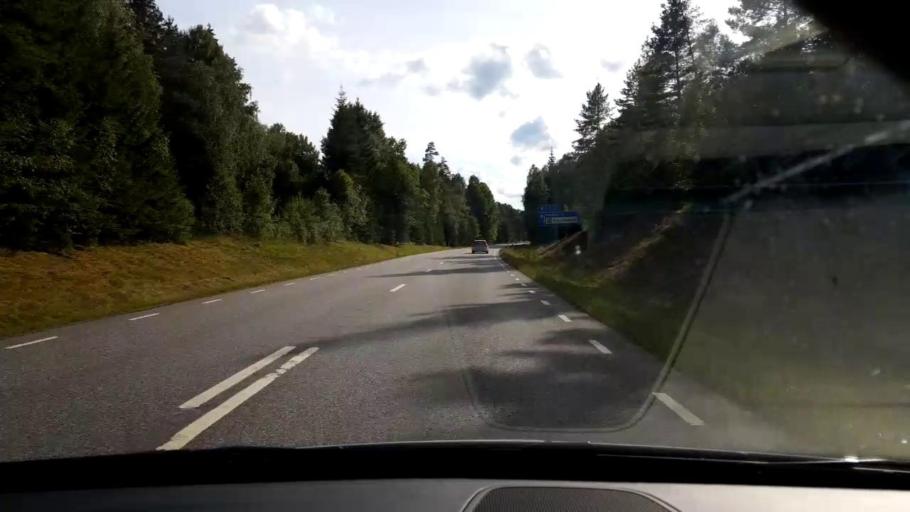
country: SE
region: Joenkoeping
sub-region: Savsjo Kommun
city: Vrigstad
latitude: 57.3301
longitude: 14.3475
